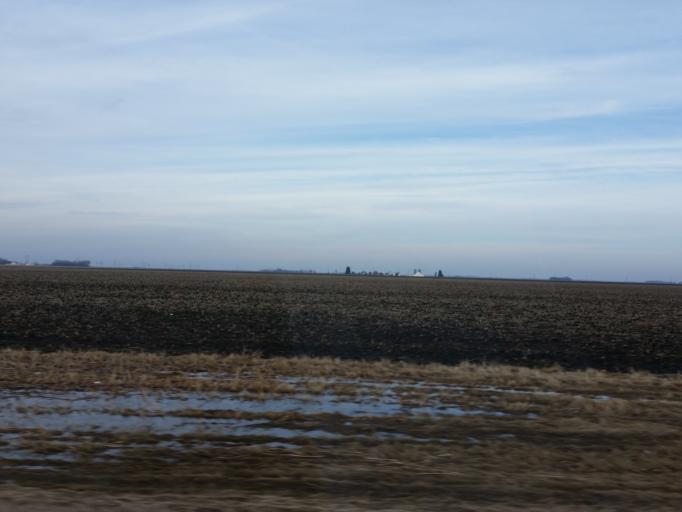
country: US
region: North Dakota
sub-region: Cass County
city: Casselton
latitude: 46.9453
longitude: -97.2199
